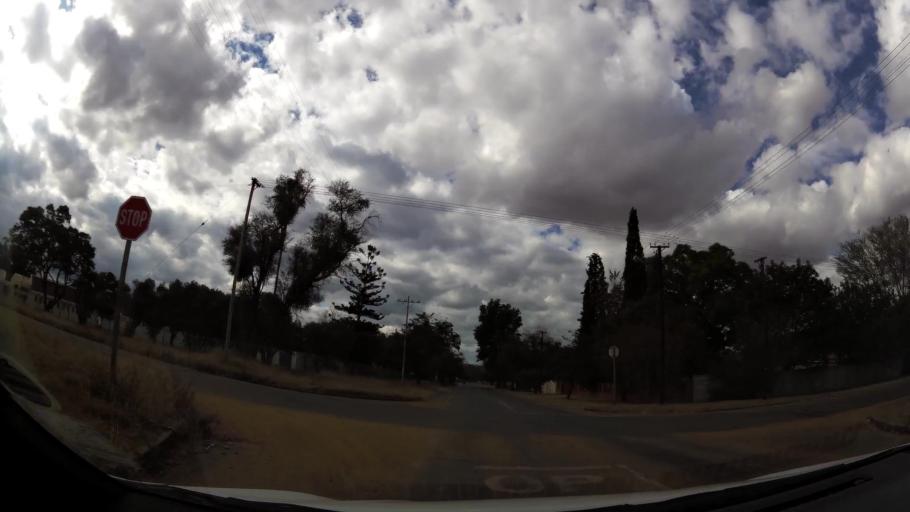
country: ZA
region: Limpopo
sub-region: Waterberg District Municipality
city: Modimolle
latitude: -24.7049
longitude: 28.4031
